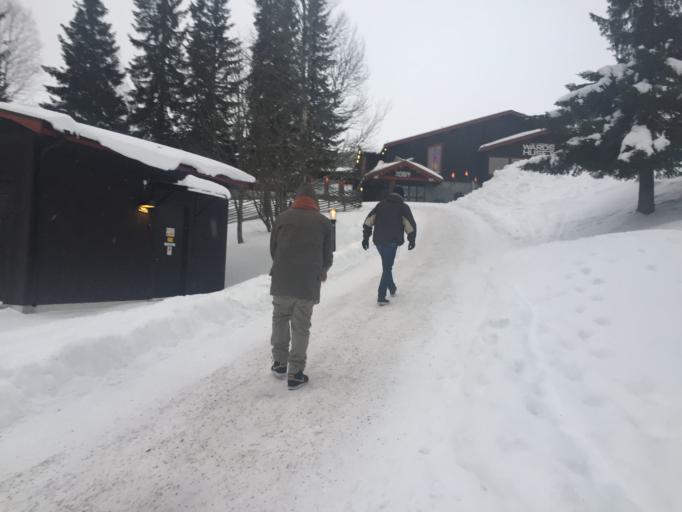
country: SE
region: Dalarna
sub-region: Malung-Saelens kommun
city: Malung
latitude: 61.1607
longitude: 13.1891
